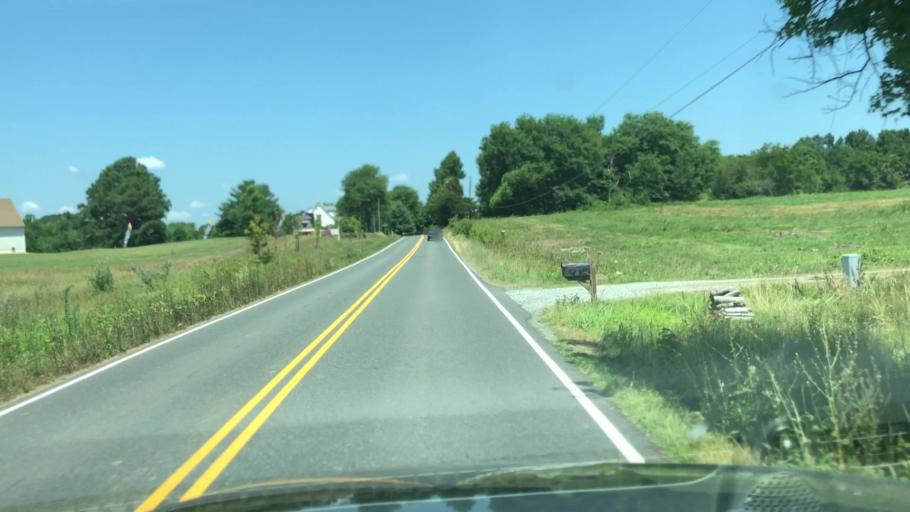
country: US
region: Virginia
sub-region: Stafford County
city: Falmouth
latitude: 38.4114
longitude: -77.5681
